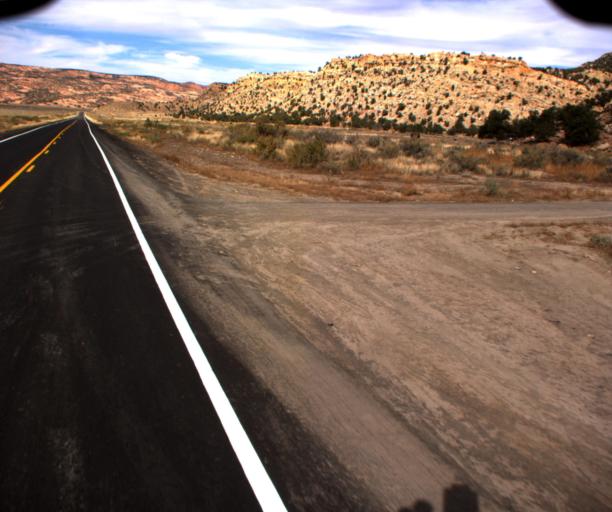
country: US
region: Arizona
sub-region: Navajo County
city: Kayenta
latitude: 36.5946
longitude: -110.4723
